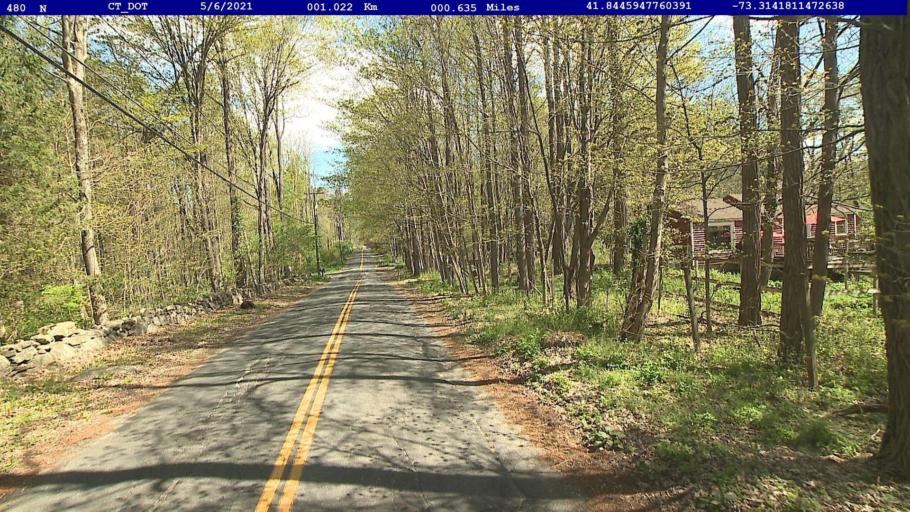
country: US
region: Connecticut
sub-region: Litchfield County
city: Litchfield
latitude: 41.8446
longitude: -73.3141
